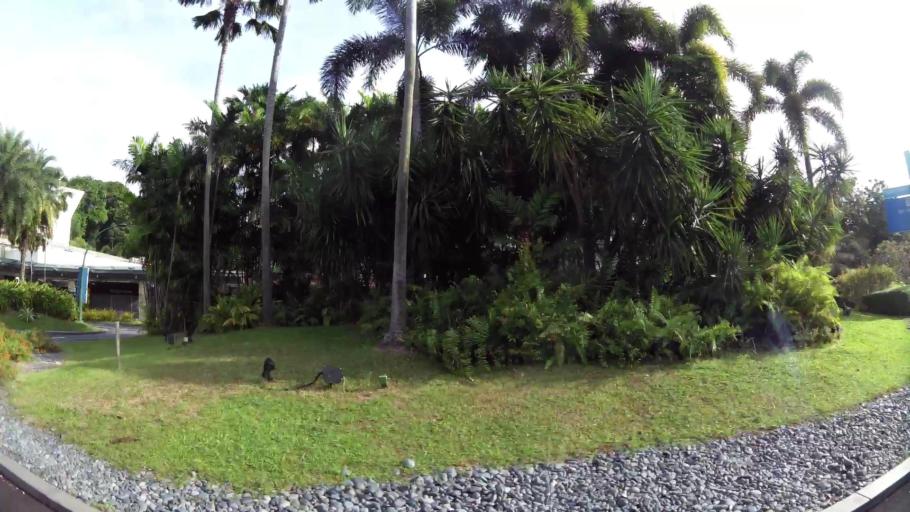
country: SG
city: Singapore
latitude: 1.2511
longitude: 103.8182
